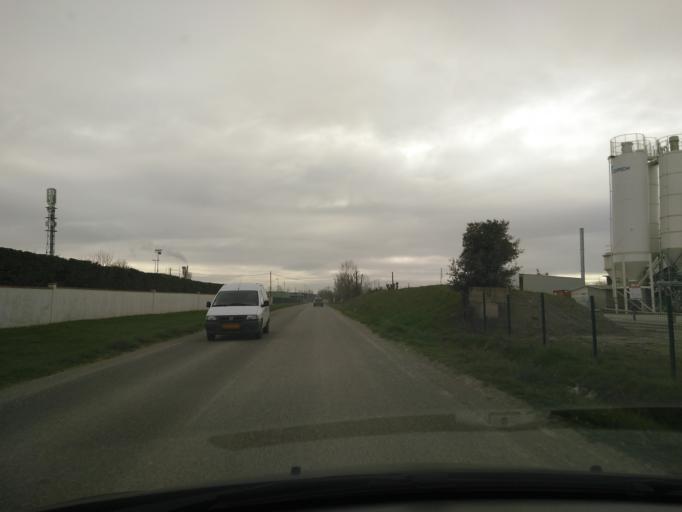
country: FR
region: Midi-Pyrenees
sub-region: Departement de la Haute-Garonne
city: Cugnaux
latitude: 43.5326
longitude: 1.3662
